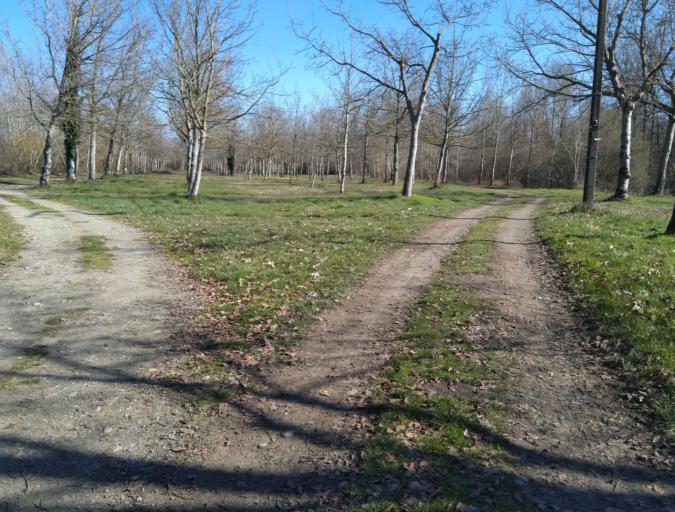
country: FR
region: Midi-Pyrenees
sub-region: Departement des Hautes-Pyrenees
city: Bazet
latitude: 43.3067
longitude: 0.0915
